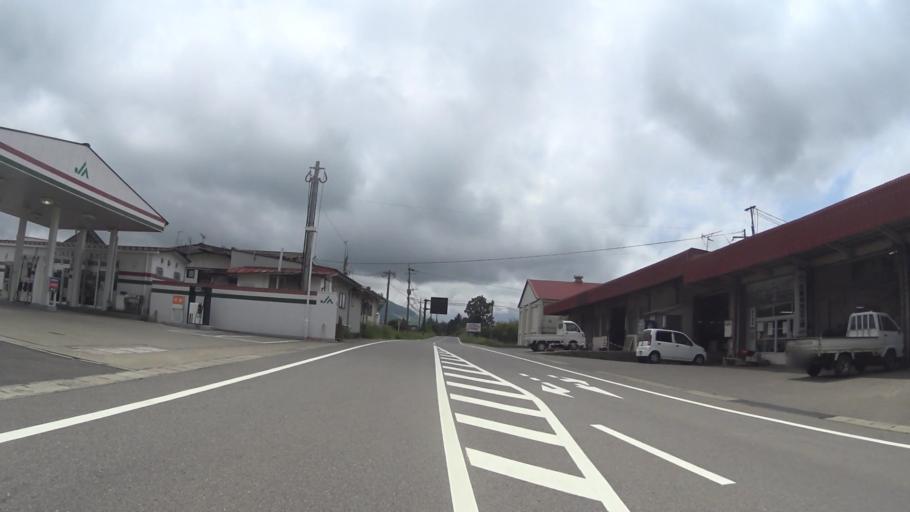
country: JP
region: Oita
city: Tsukawaki
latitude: 33.1572
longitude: 131.2409
